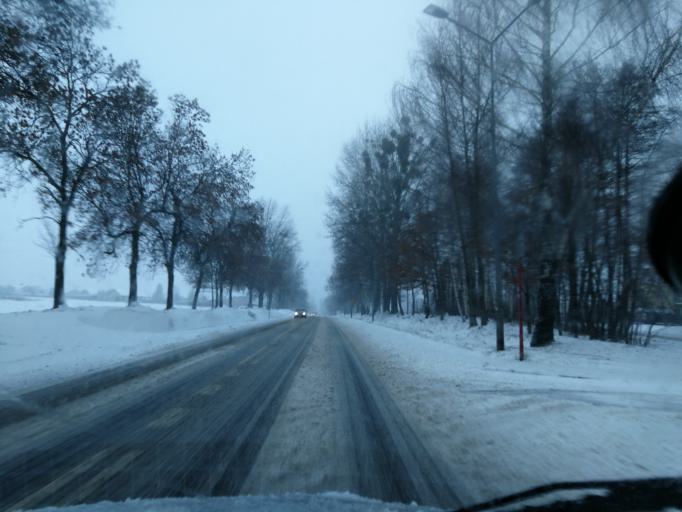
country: PL
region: Silesian Voivodeship
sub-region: Powiat pszczynski
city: Pszczyna
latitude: 49.9871
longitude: 18.9227
